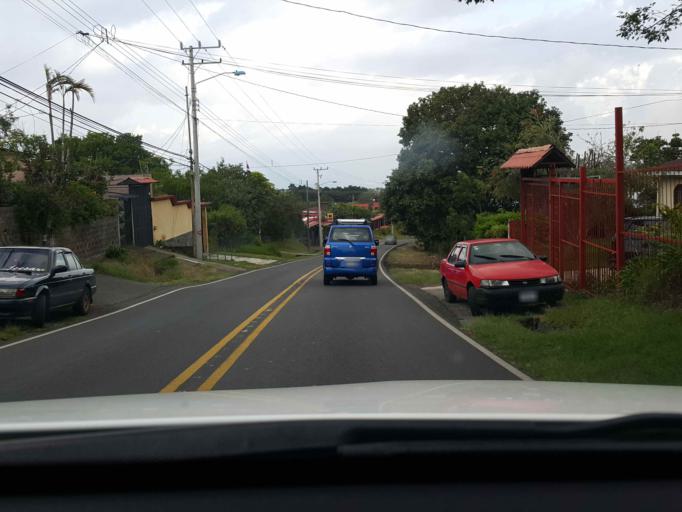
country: CR
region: Heredia
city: San Josecito
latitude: 10.0329
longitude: -84.0914
